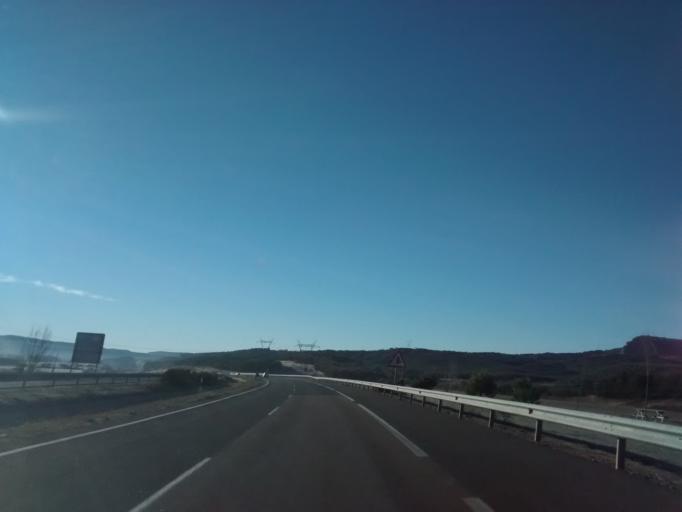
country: ES
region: Castille and Leon
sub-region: Provincia de Palencia
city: Aguilar de Campoo
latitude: 42.7530
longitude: -4.2934
